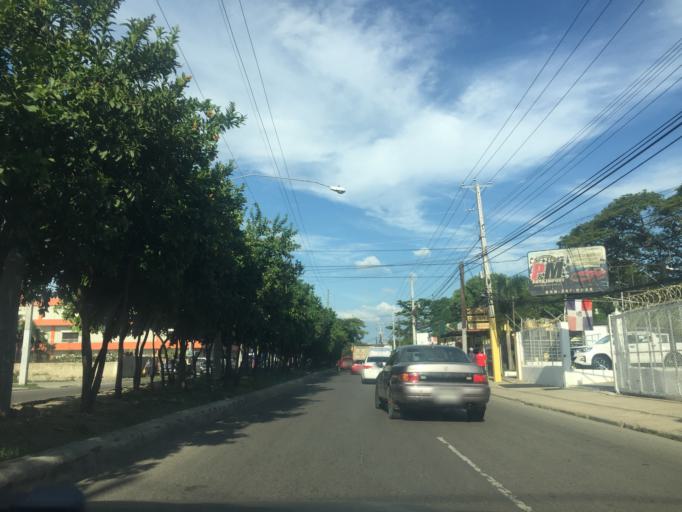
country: DO
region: Santiago
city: Santiago de los Caballeros
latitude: 19.4402
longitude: -70.7244
